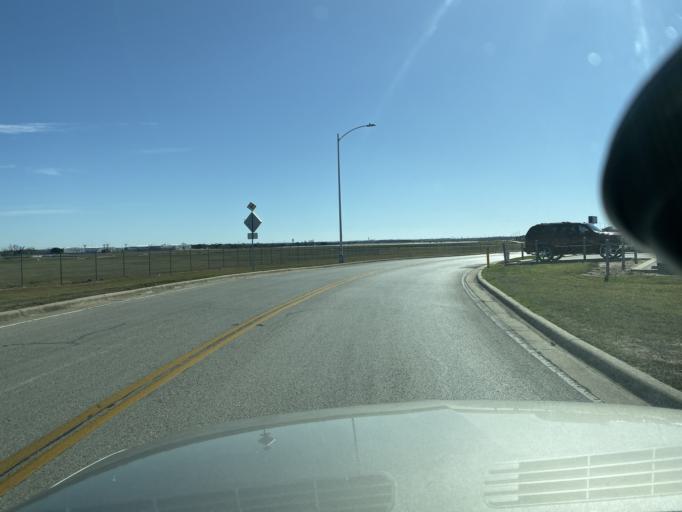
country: US
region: Texas
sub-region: Travis County
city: Hornsby Bend
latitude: 30.2097
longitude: -97.6606
